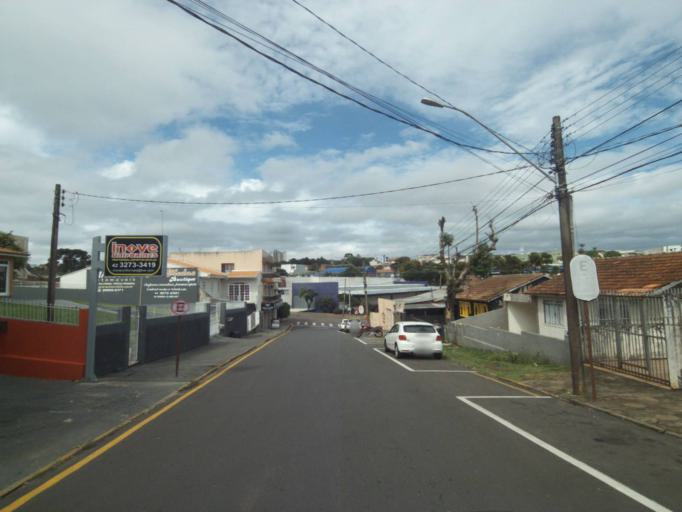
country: BR
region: Parana
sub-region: Telemaco Borba
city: Telemaco Borba
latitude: -24.3291
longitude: -50.6257
